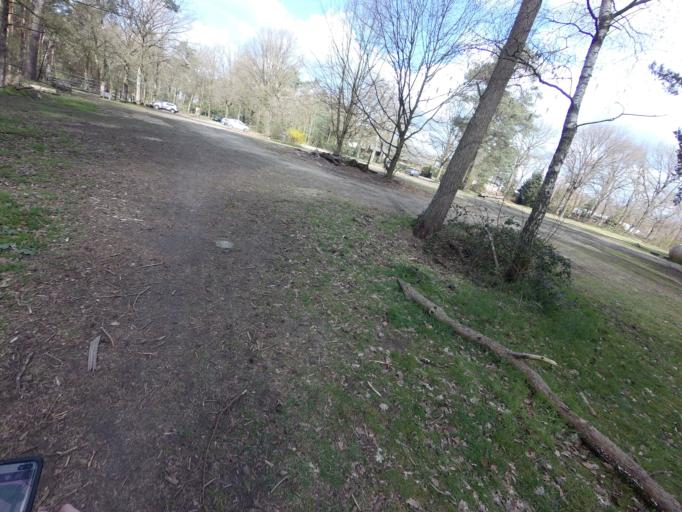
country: NL
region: Limburg
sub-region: Gemeente Roerdalen
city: Herkenbosch
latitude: 51.1652
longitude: 6.0855
